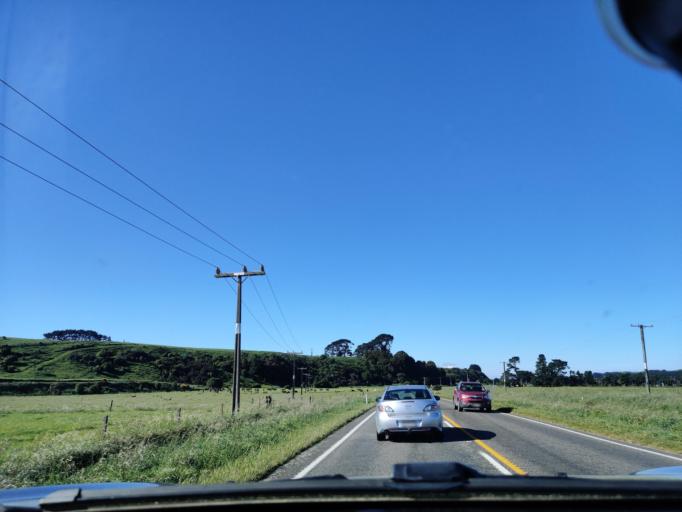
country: NZ
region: Manawatu-Wanganui
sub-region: Palmerston North City
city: Palmerston North
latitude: -40.5862
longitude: 175.7226
